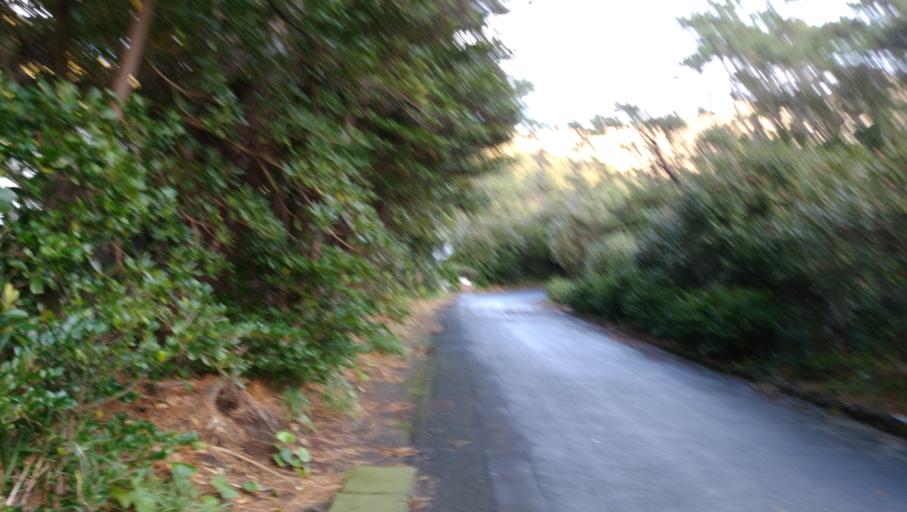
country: JP
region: Kagoshima
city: Makurazaki
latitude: 30.7837
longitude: 130.2798
